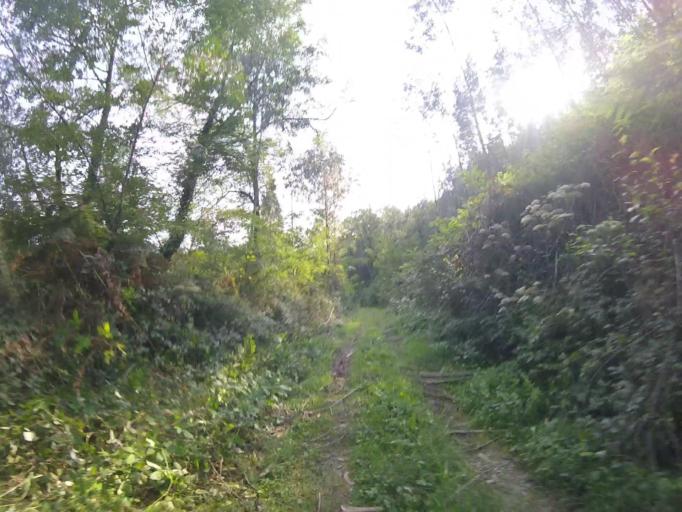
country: ES
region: Navarre
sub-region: Provincia de Navarra
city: Arano
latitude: 43.2287
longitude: -1.9334
